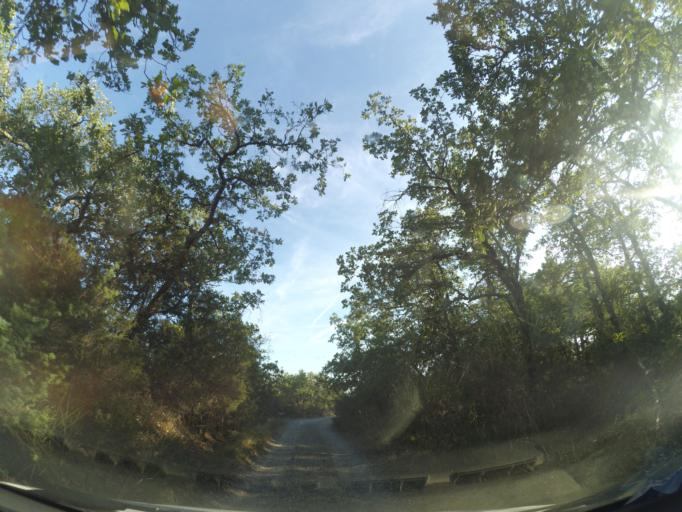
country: IT
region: Tuscany
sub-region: Province of Arezzo
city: Castiglion Fibocchi
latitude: 43.5375
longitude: 11.7874
